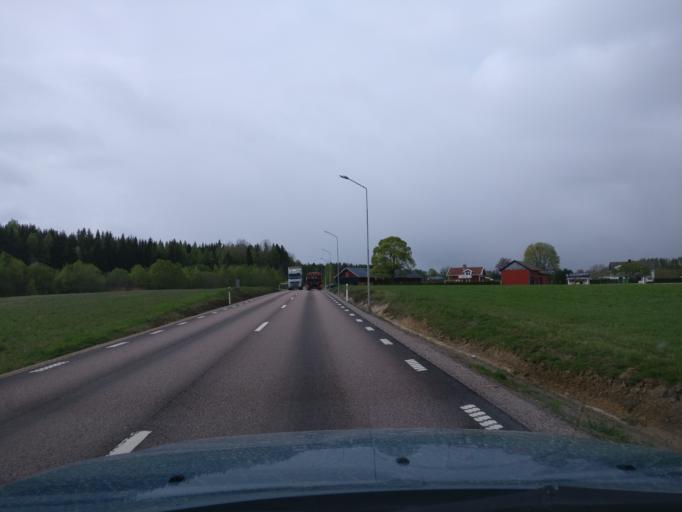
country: SE
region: Vaermland
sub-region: Forshaga Kommun
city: Deje
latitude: 59.6223
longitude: 13.4454
